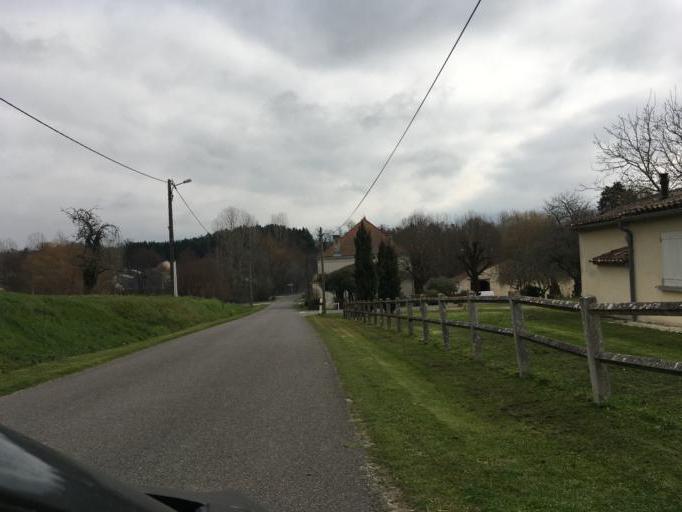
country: FR
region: Poitou-Charentes
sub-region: Departement de la Charente-Maritime
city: Mirambeau
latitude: 45.3267
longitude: -0.5740
